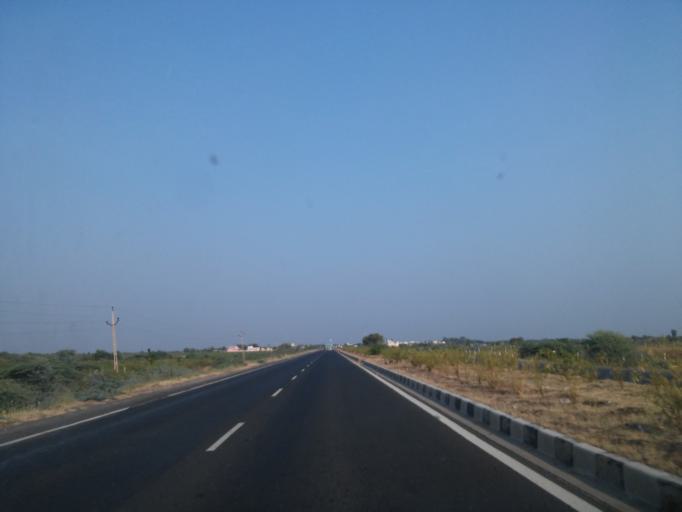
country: IN
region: Gujarat
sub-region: Surendranagar
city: Lakhtar
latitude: 23.0613
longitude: 71.7343
